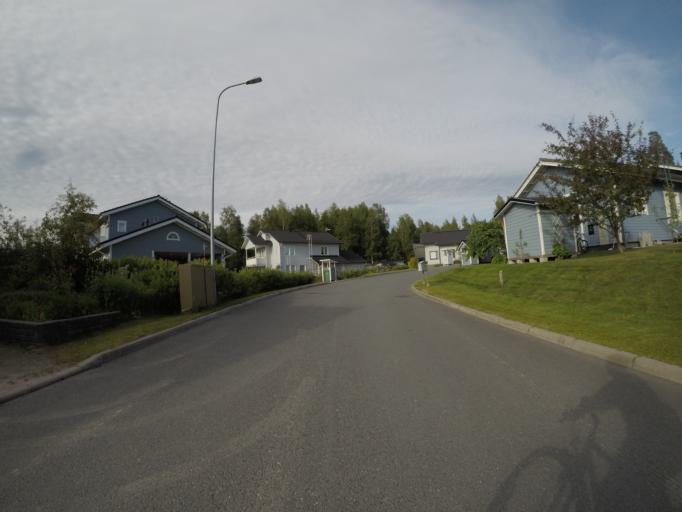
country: FI
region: Haeme
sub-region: Haemeenlinna
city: Parola
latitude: 60.9768
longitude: 24.3847
